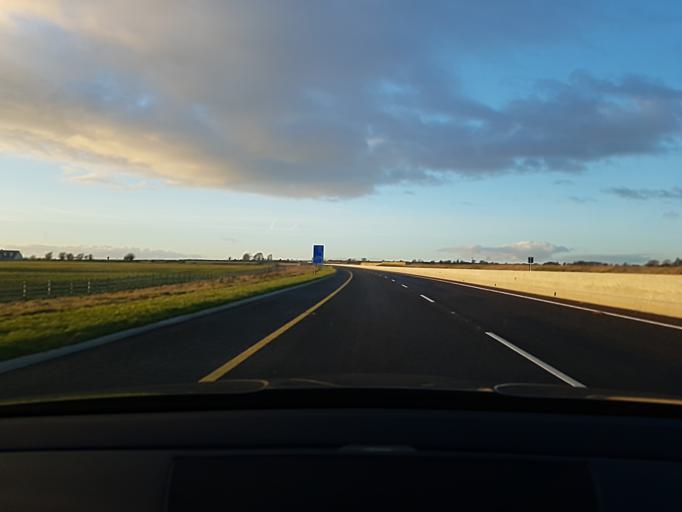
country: IE
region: Connaught
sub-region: County Galway
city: Athenry
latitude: 53.3950
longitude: -8.8055
